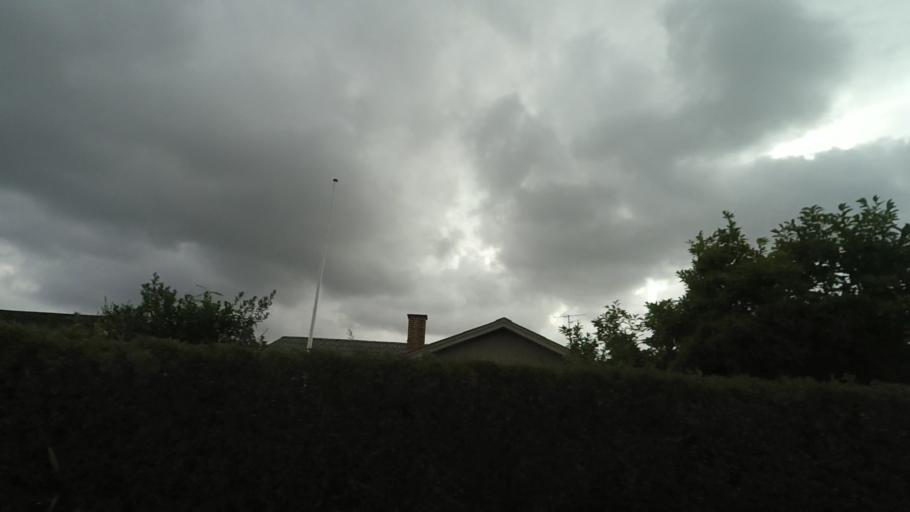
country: DK
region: Central Jutland
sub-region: Syddjurs Kommune
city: Ryomgard
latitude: 56.4102
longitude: 10.5754
